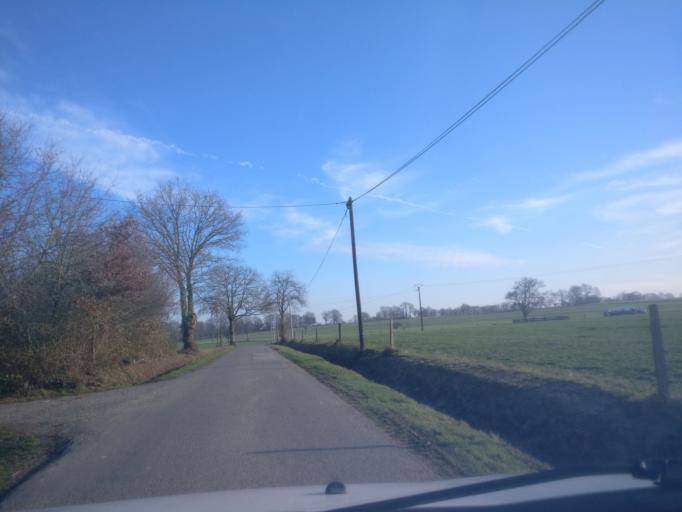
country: FR
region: Brittany
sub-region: Departement d'Ille-et-Vilaine
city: Livre-sur-Changeon
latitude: 48.2141
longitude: -1.3057
